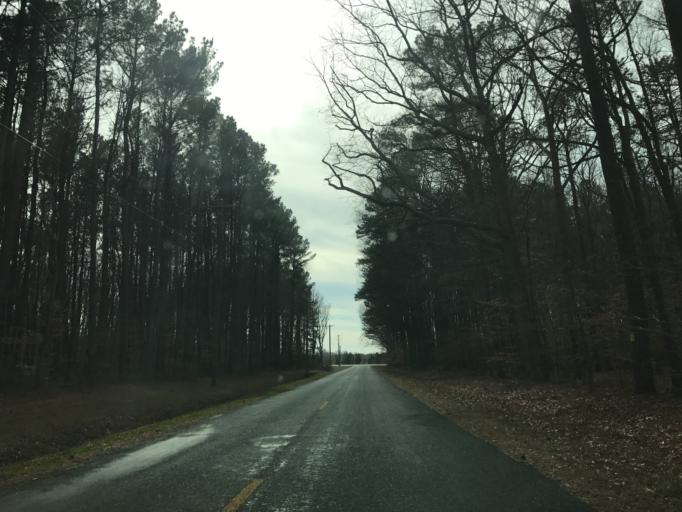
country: US
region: Maryland
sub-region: Queen Anne's County
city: Centreville
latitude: 39.0480
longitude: -76.1318
